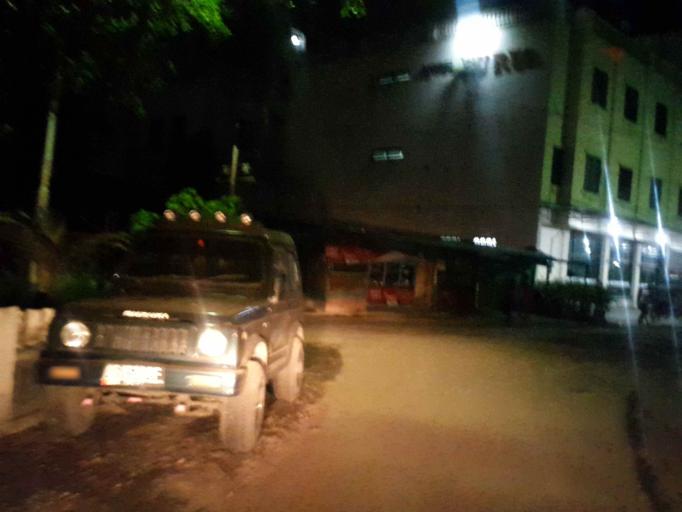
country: ID
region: Central Java
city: Surakarta
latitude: -7.5539
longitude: 110.8207
